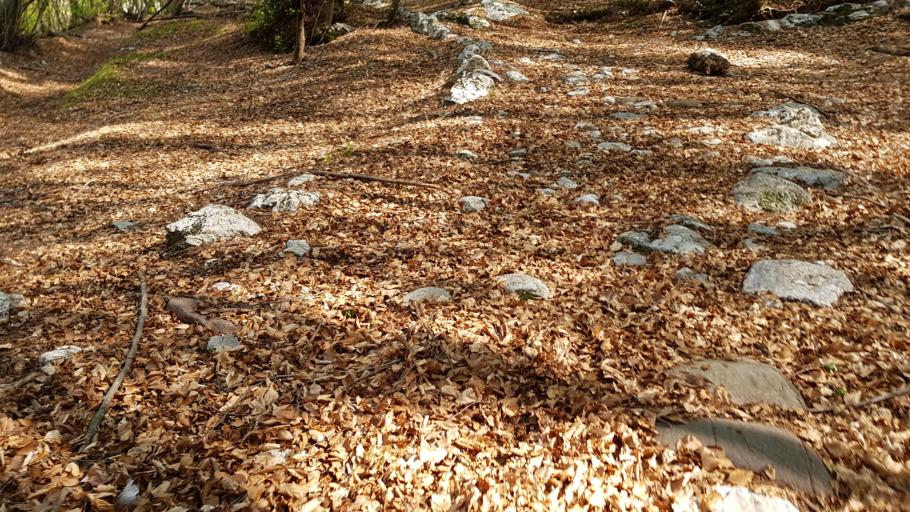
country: IT
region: Trentino-Alto Adige
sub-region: Provincia di Trento
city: Vezzano
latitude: 46.0730
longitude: 11.0111
